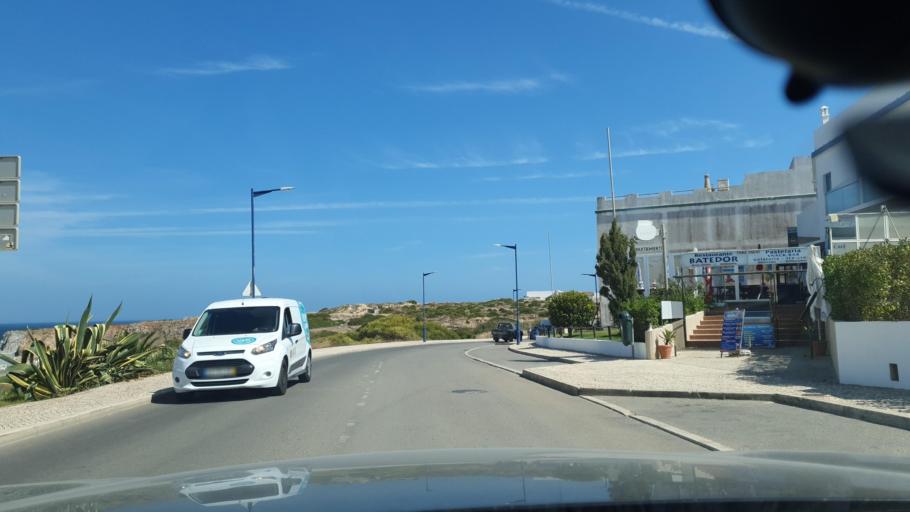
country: PT
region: Faro
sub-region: Vila do Bispo
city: Sagres
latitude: 37.0099
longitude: -8.9323
